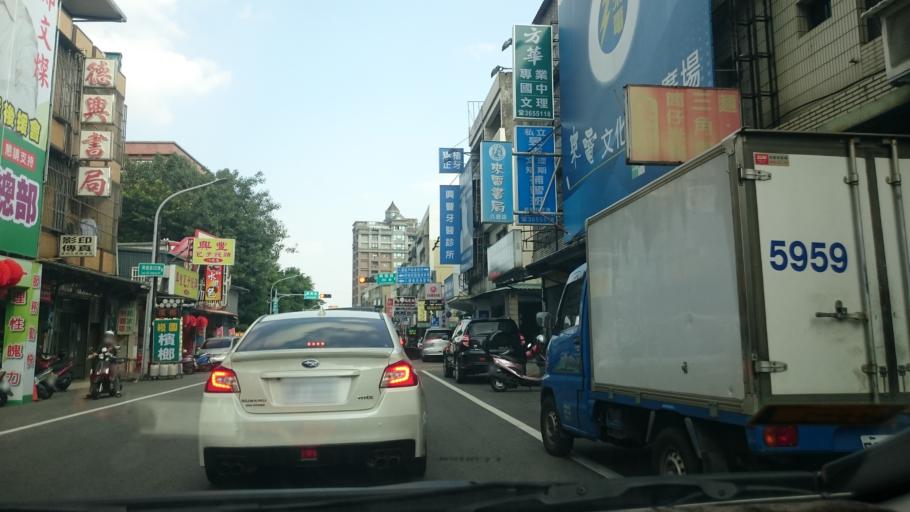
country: TW
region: Taiwan
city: Daxi
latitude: 24.9293
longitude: 121.2858
